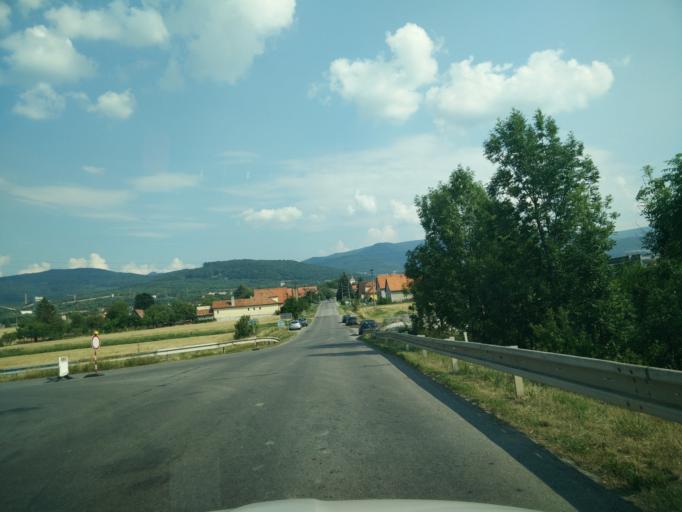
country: SK
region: Nitriansky
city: Prievidza
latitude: 48.7362
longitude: 18.6131
